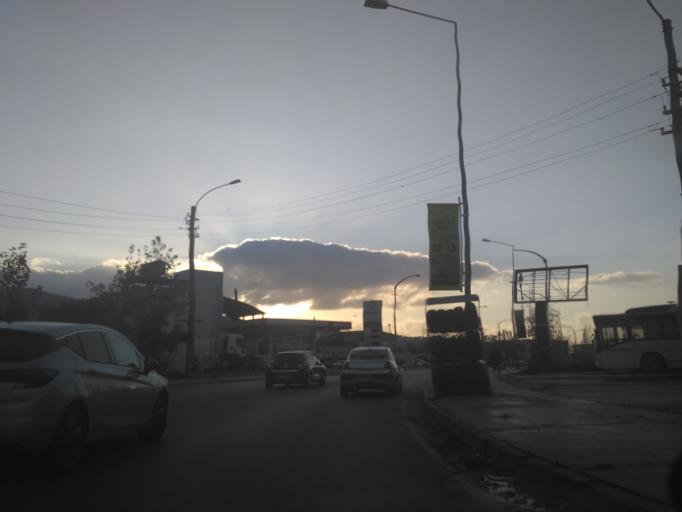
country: TR
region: Izmir
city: Buca
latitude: 38.4284
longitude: 27.2118
